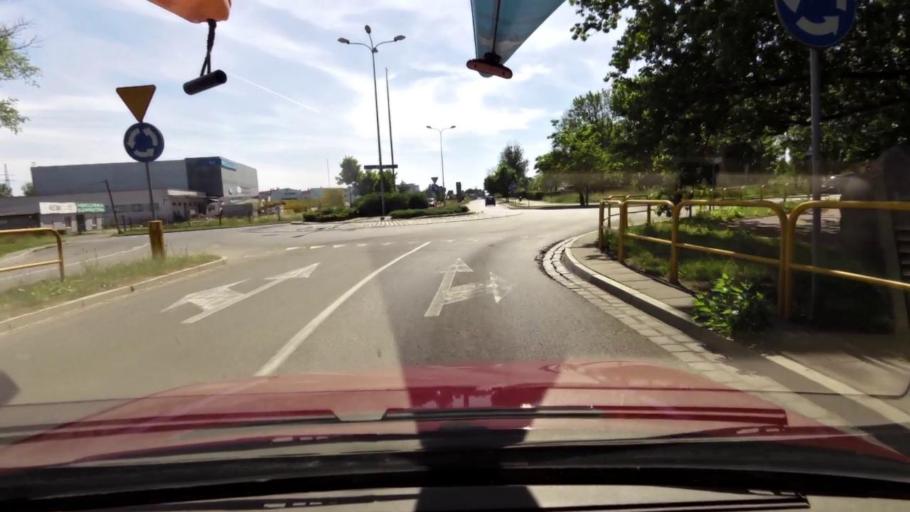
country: PL
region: Pomeranian Voivodeship
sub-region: Powiat slupski
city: Kobylnica
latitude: 54.4503
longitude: 17.0138
